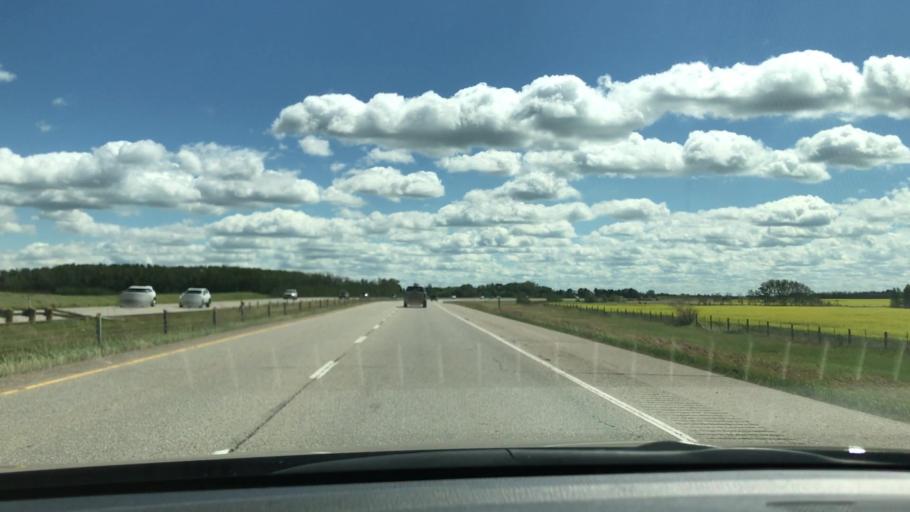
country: CA
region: Alberta
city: Leduc
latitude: 53.2475
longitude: -113.5617
